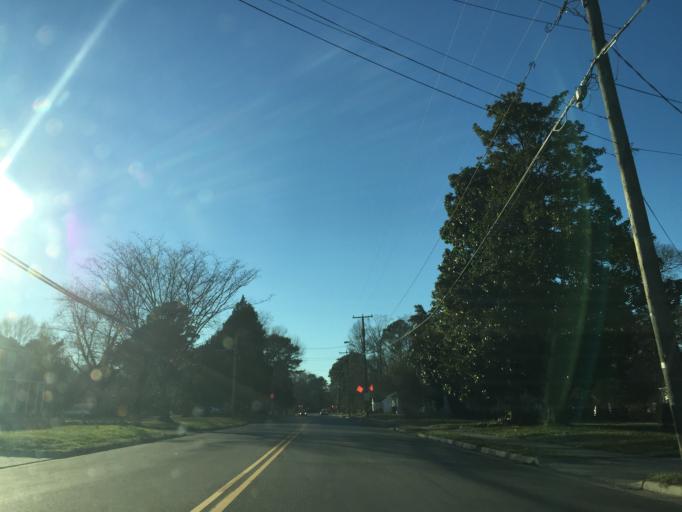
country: US
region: Virginia
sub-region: City of Newport News
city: Newport News
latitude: 37.0888
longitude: -76.5065
